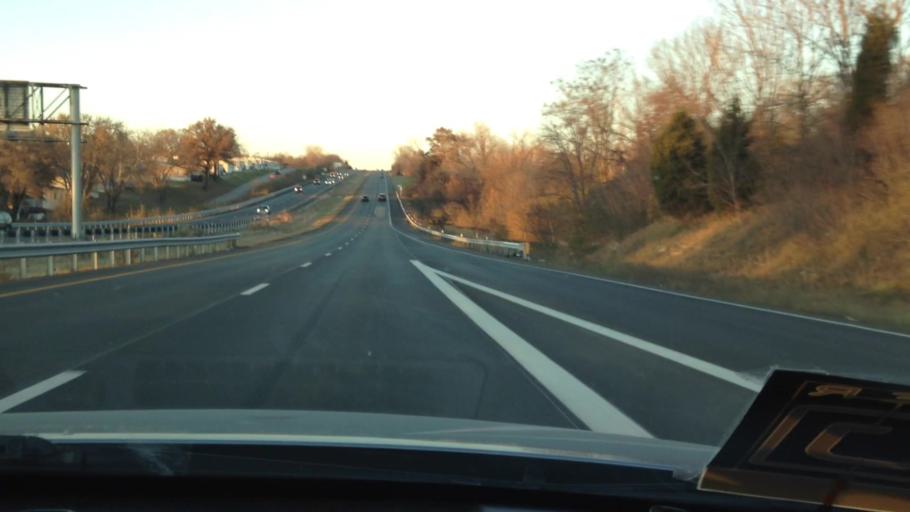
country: US
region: Missouri
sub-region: Platte County
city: Riverside
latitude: 39.1977
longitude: -94.5898
